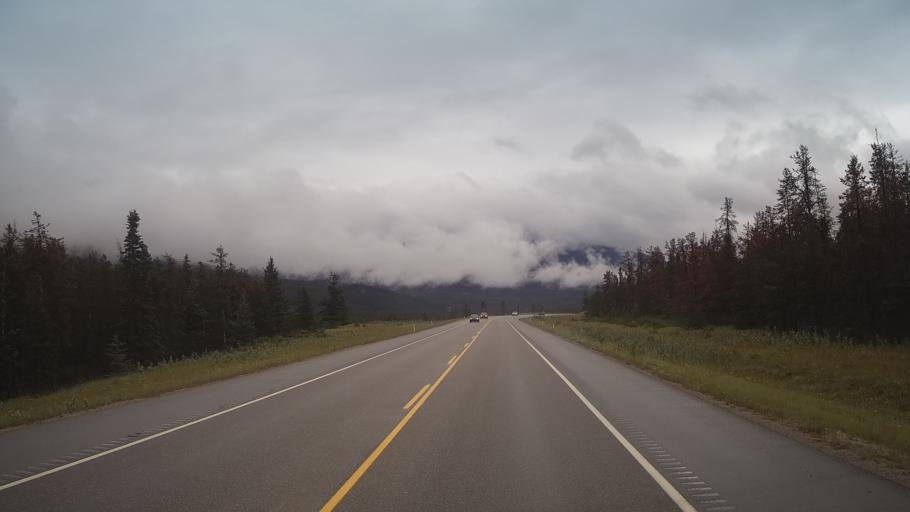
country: CA
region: Alberta
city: Jasper Park Lodge
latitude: 52.9514
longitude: -118.0419
